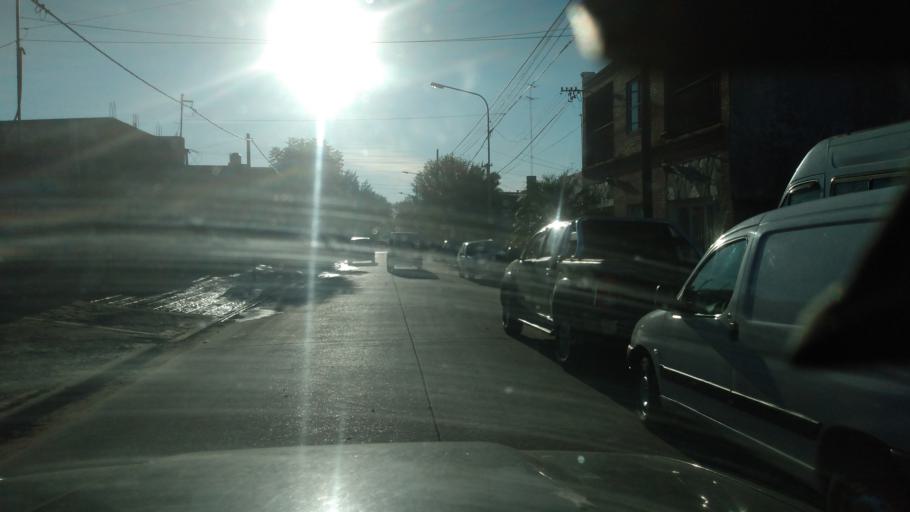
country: AR
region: Buenos Aires
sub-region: Partido de Lujan
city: Lujan
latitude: -34.5691
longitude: -59.0923
